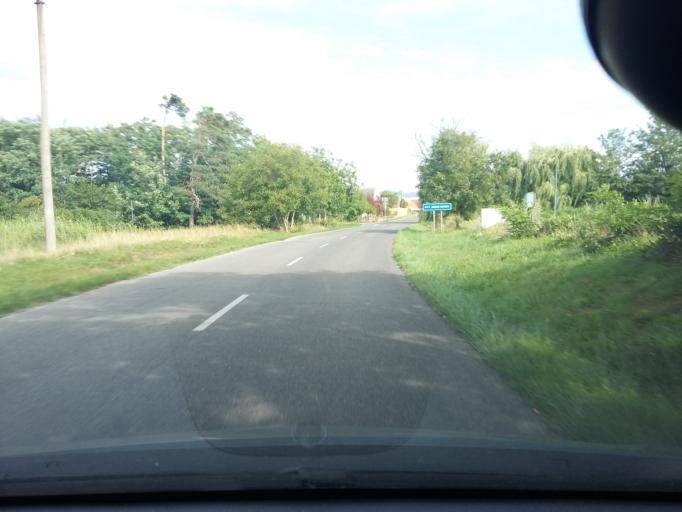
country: SK
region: Trnavsky
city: Gbely
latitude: 48.5727
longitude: 17.2108
